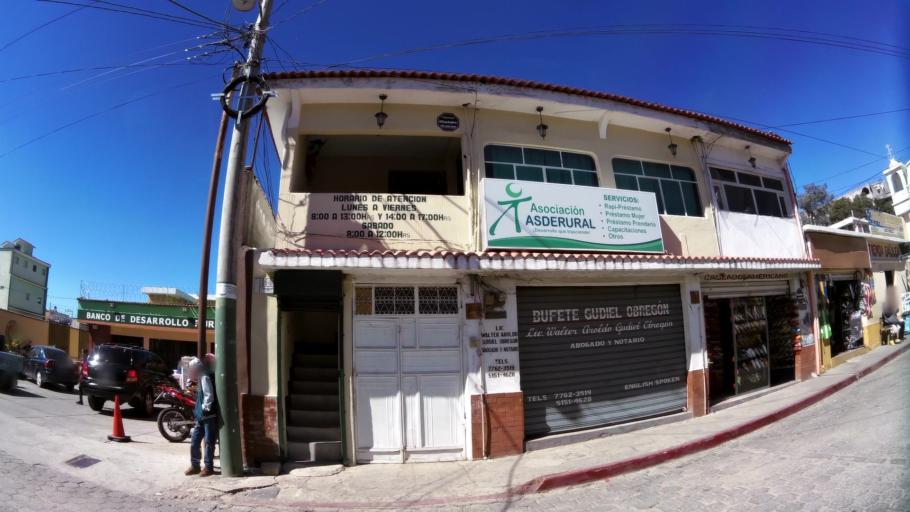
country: GT
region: Solola
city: Solola
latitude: 14.7735
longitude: -91.1828
